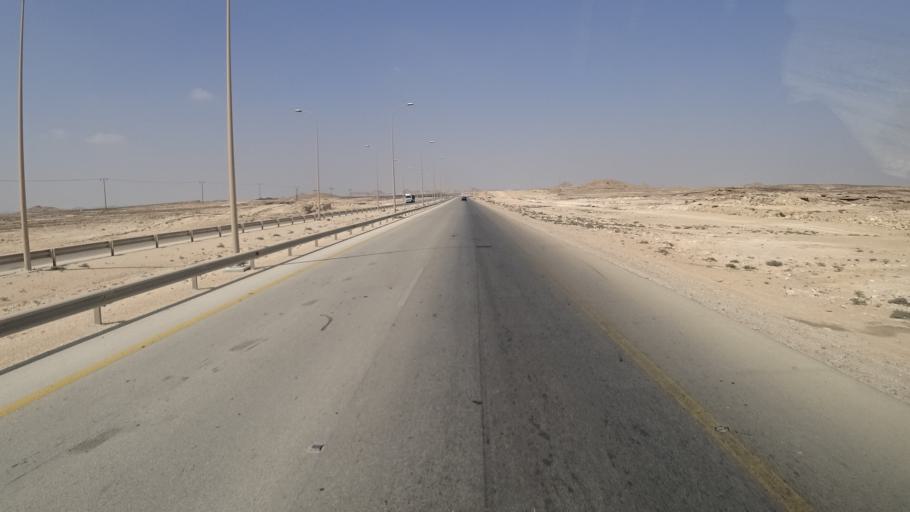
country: OM
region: Zufar
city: Salalah
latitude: 17.3467
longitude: 54.0789
